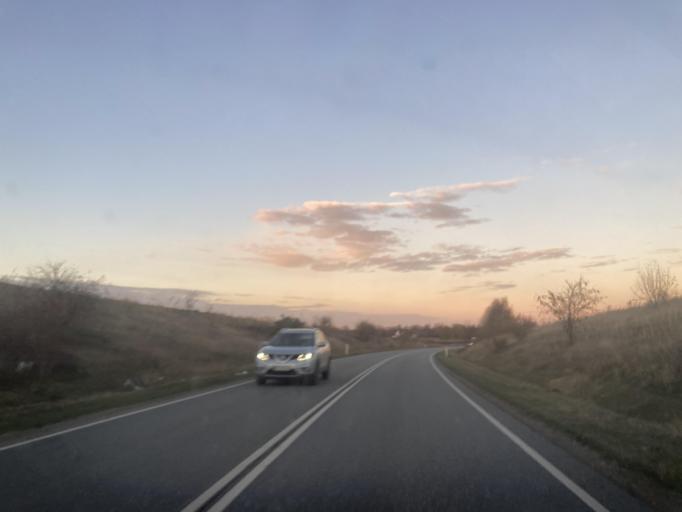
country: DK
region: Capital Region
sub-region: Gribskov Kommune
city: Graested
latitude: 56.0738
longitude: 12.2772
